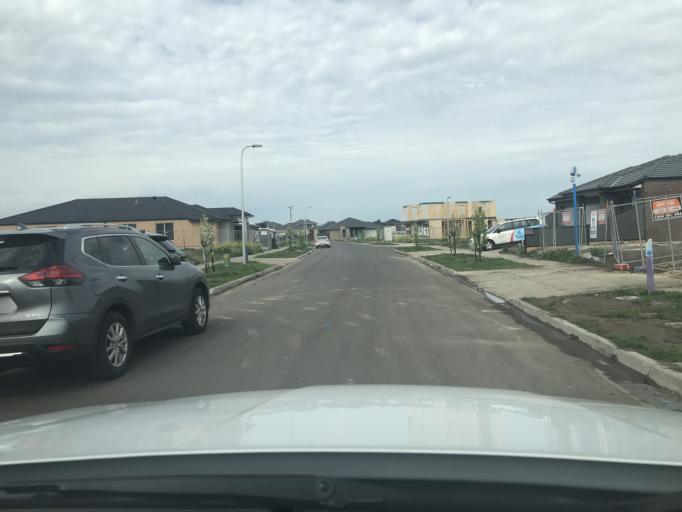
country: AU
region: Victoria
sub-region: Hume
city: Roxburgh Park
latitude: -37.6020
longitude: 144.8989
